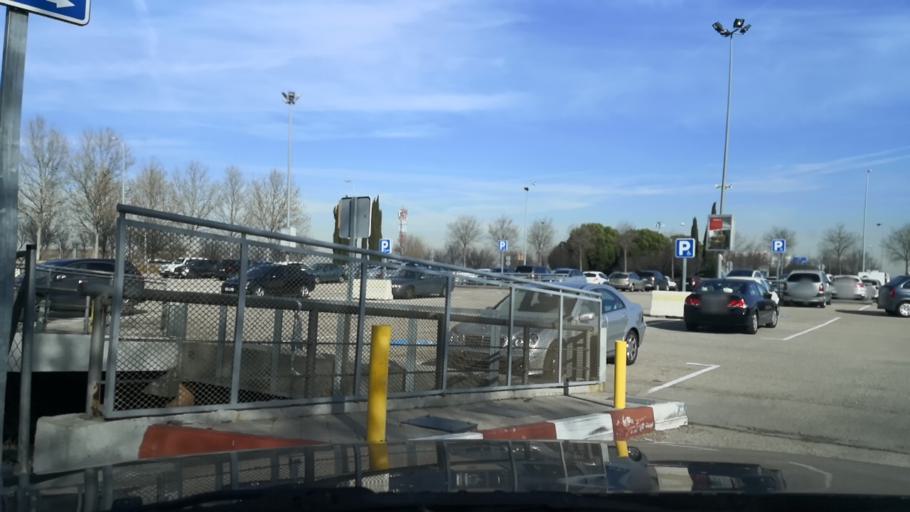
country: ES
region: Madrid
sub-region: Provincia de Madrid
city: Hortaleza
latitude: 40.4707
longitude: -3.6150
